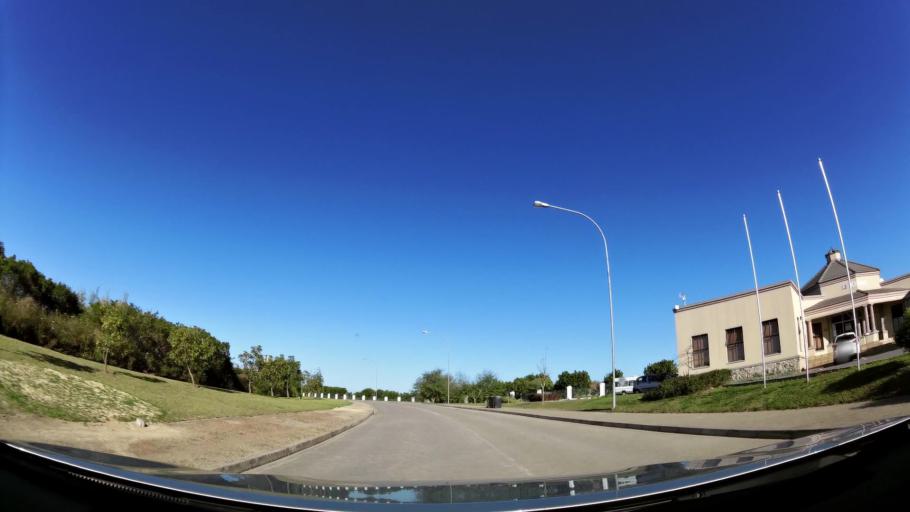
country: ZA
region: Western Cape
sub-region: Eden District Municipality
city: George
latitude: -33.9661
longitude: 22.4302
